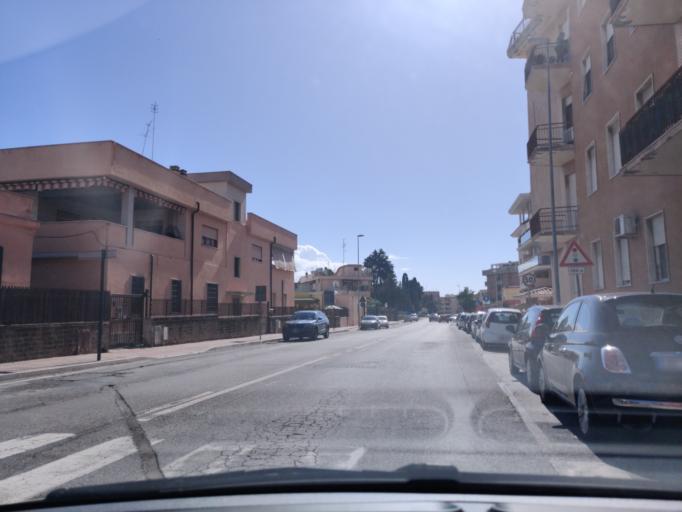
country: IT
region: Latium
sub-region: Citta metropolitana di Roma Capitale
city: Civitavecchia
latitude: 42.0920
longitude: 11.8068
